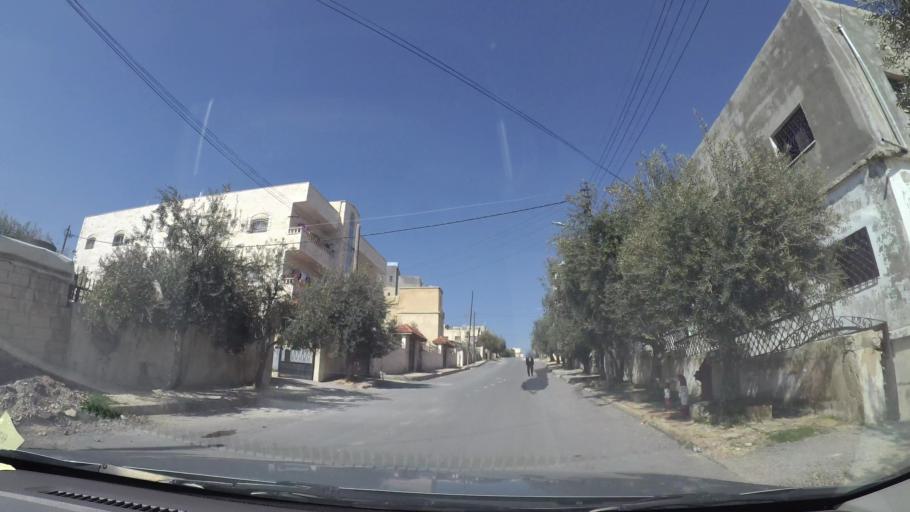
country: JO
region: Amman
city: Al Bunayyat ash Shamaliyah
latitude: 31.9033
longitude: 35.9054
